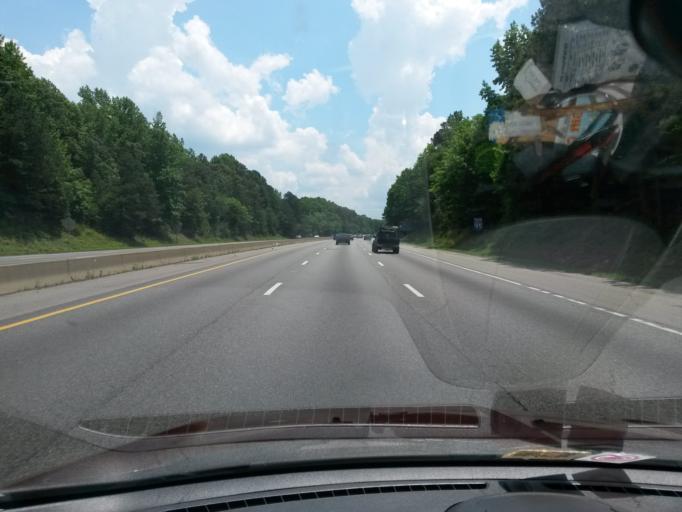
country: US
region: Virginia
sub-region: Chesterfield County
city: Chester
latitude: 37.3727
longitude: -77.4054
